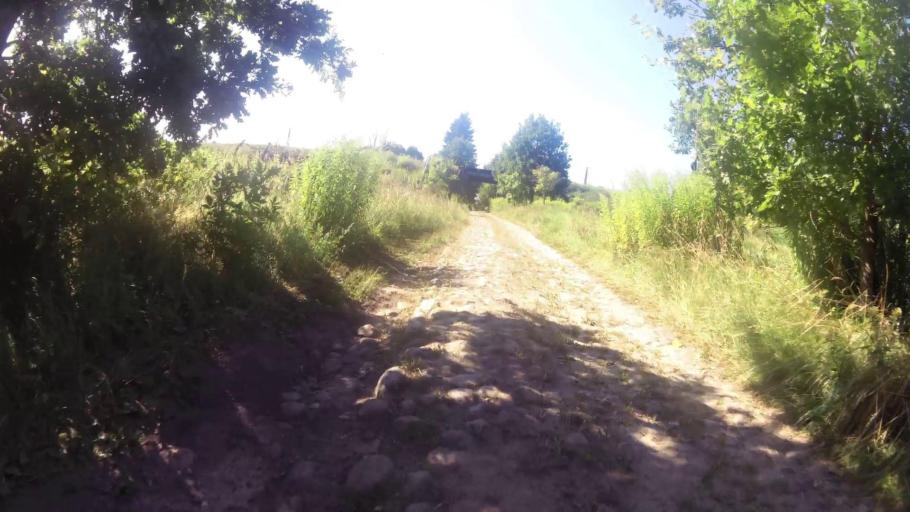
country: PL
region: West Pomeranian Voivodeship
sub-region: Powiat drawski
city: Drawsko Pomorskie
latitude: 53.5225
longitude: 15.7063
